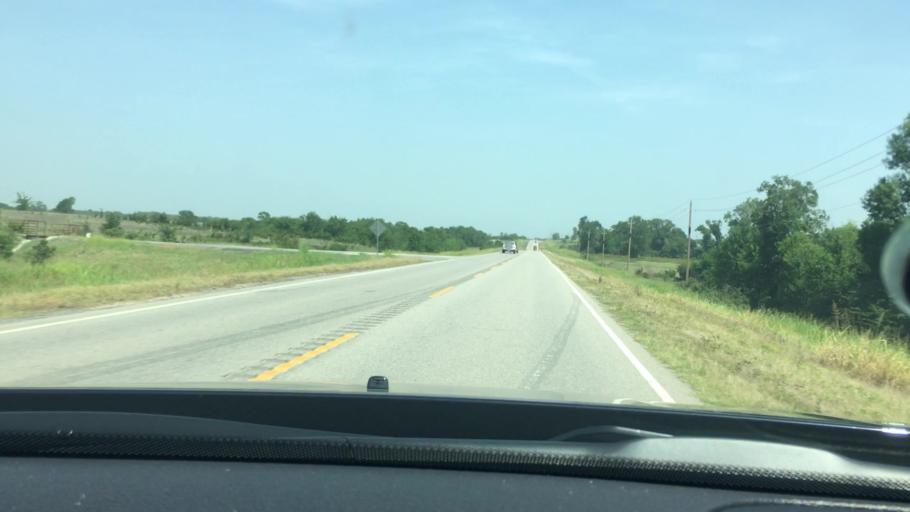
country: US
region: Oklahoma
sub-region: Coal County
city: Coalgate
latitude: 34.4480
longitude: -96.2081
